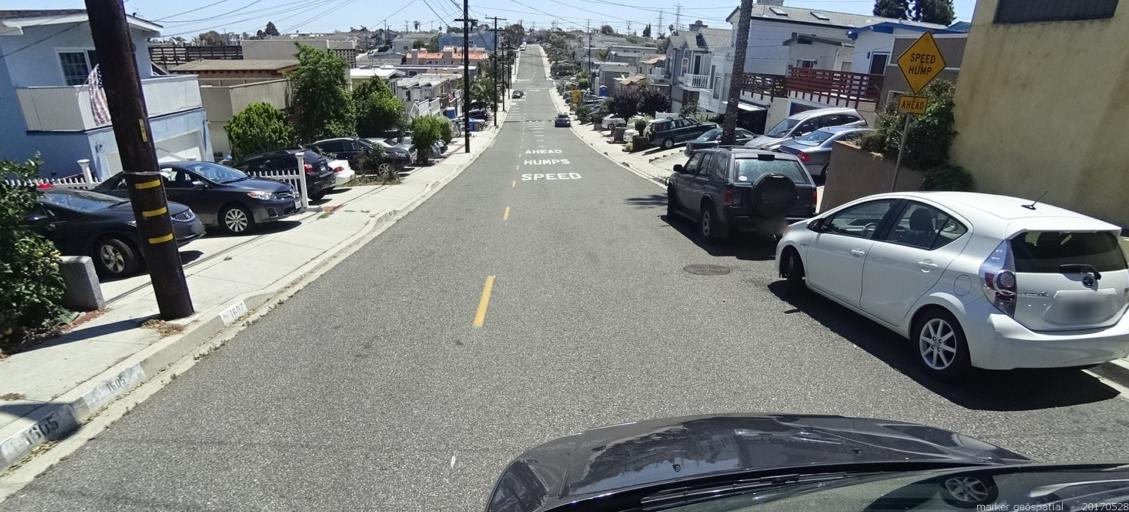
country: US
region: California
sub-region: Los Angeles County
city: Redondo Beach
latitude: 33.8581
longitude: -118.3848
